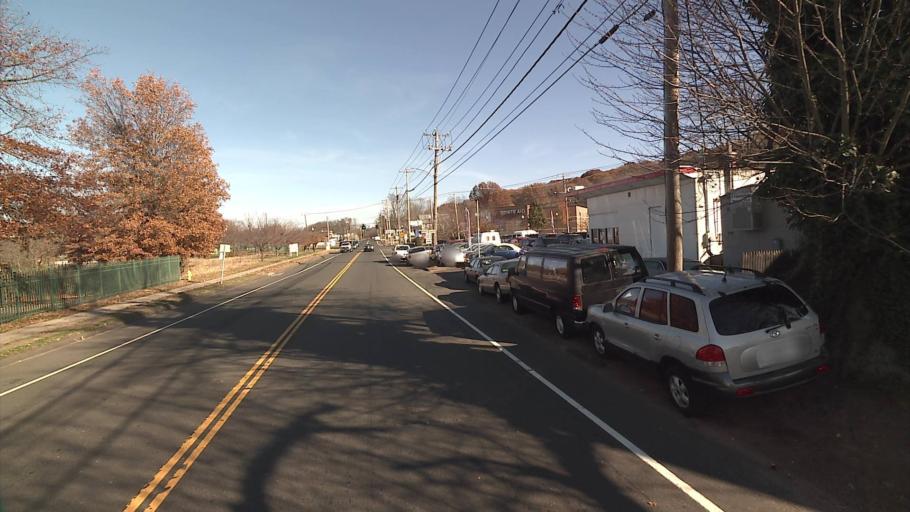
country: US
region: Connecticut
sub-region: New Haven County
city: North Haven
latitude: 41.3394
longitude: -72.8643
